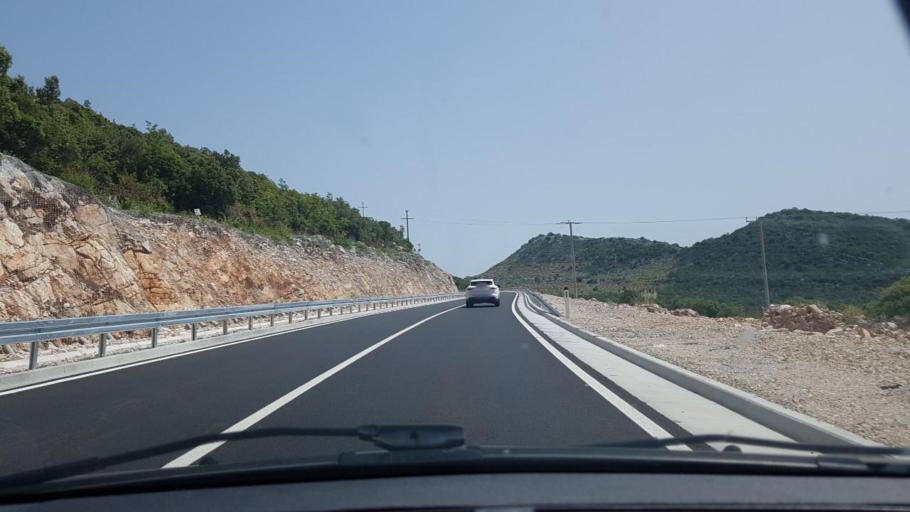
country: HR
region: Dubrovacko-Neretvanska
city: Ston
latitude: 42.9506
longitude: 17.7585
